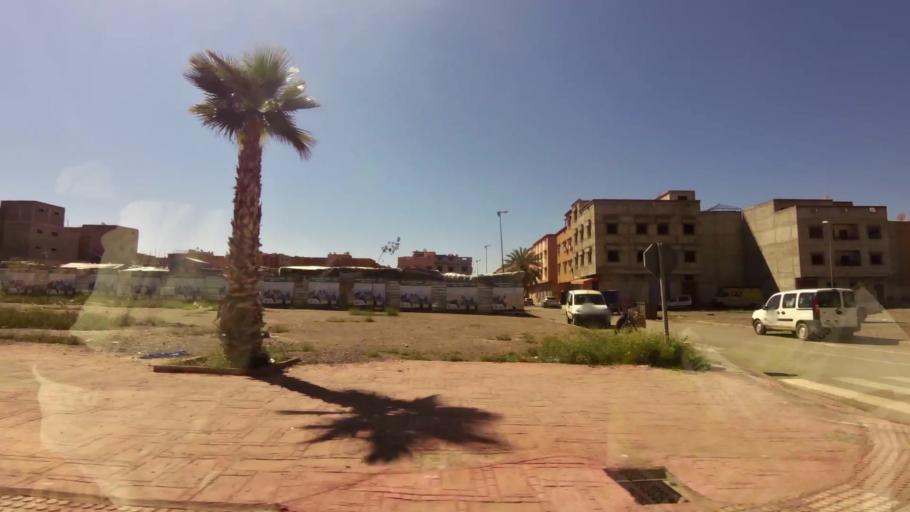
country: MA
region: Marrakech-Tensift-Al Haouz
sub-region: Marrakech
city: Marrakesh
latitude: 31.5881
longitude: -8.0593
